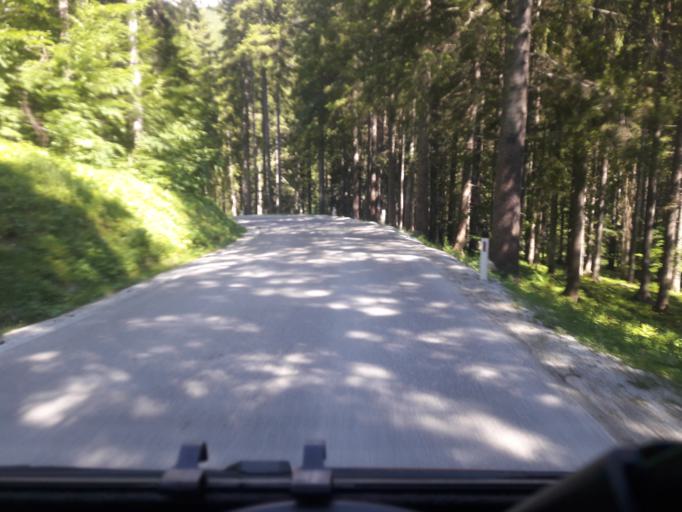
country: AT
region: Styria
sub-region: Politischer Bezirk Liezen
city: Tauplitz
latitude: 47.5774
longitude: 13.9662
